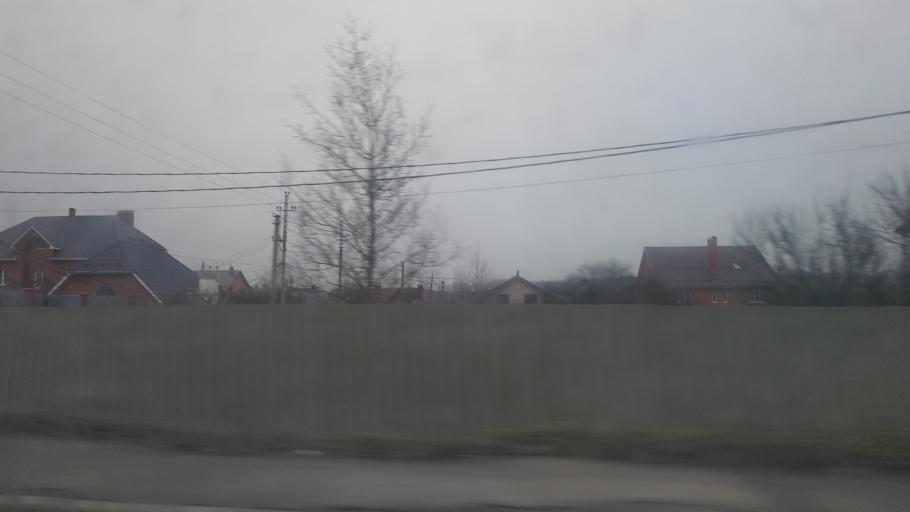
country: RU
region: Moskovskaya
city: Sheremet'yevskiy
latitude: 56.0088
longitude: 37.5445
